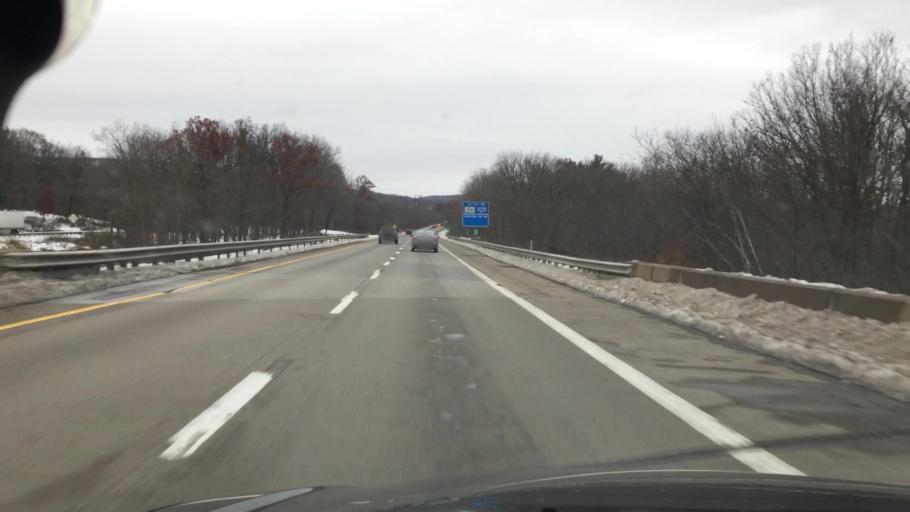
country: US
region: Pennsylvania
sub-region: Luzerne County
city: Mountain Top
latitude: 41.1118
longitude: -75.9616
